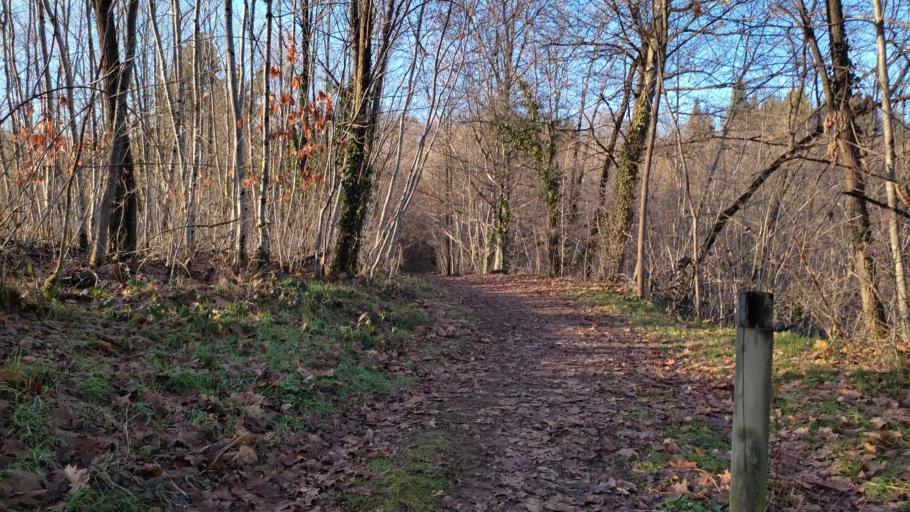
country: FR
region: Limousin
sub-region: Departement de la Haute-Vienne
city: Isle
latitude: 45.8051
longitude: 1.1844
